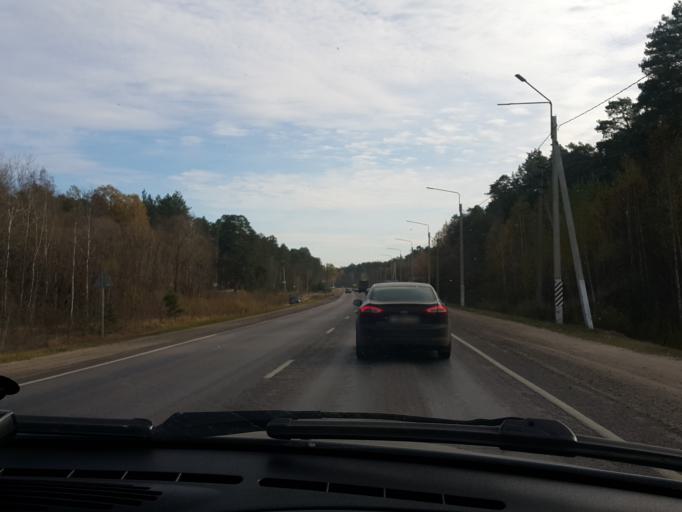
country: RU
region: Tambov
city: Donskoye
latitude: 52.7099
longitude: 41.5295
